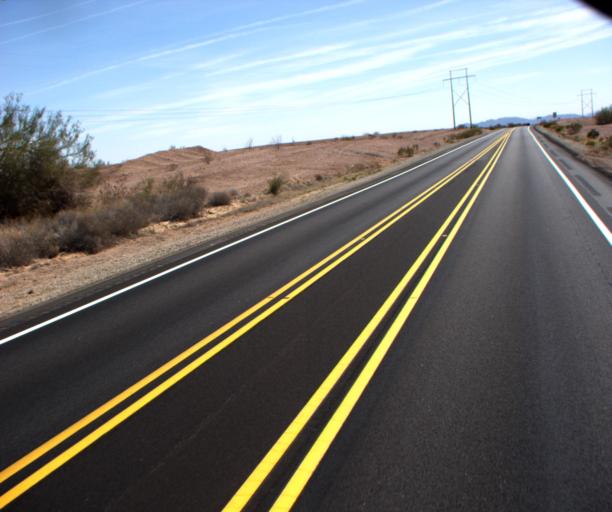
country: US
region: Arizona
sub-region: Yuma County
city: Wellton
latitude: 33.0219
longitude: -114.2871
